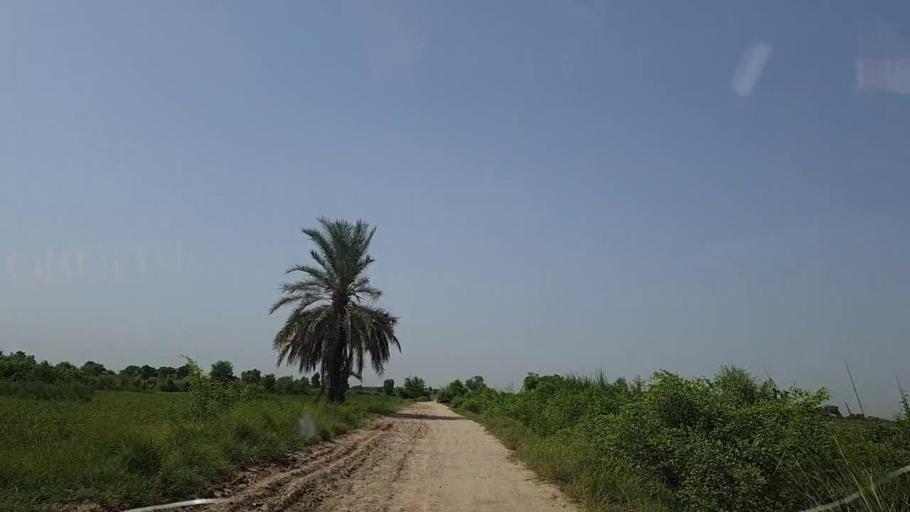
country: PK
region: Sindh
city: Naushahro Firoz
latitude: 26.8697
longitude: 68.0328
